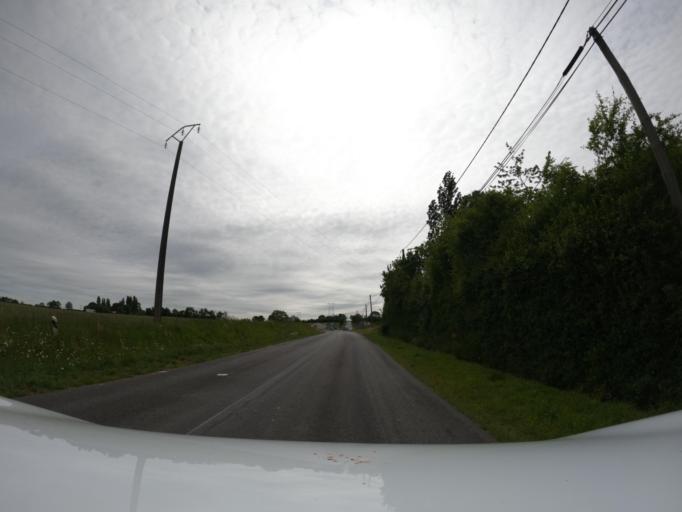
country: FR
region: Pays de la Loire
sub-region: Departement de la Vendee
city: Saint-Hilaire-des-Loges
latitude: 46.4942
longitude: -0.6641
